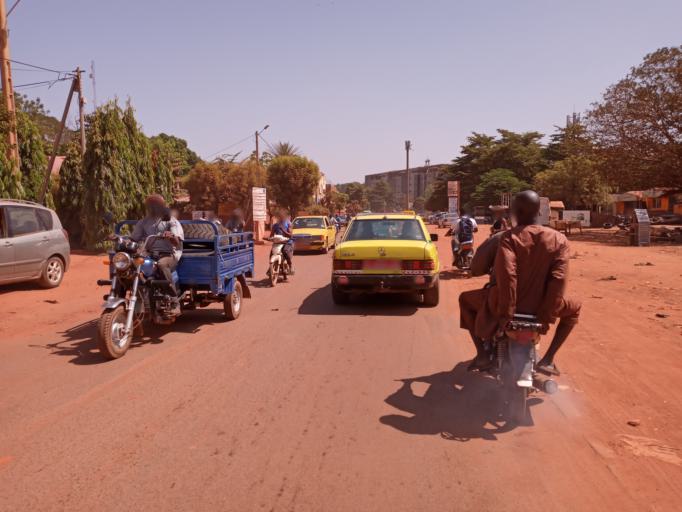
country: ML
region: Bamako
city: Bamako
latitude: 12.6140
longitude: -7.9948
